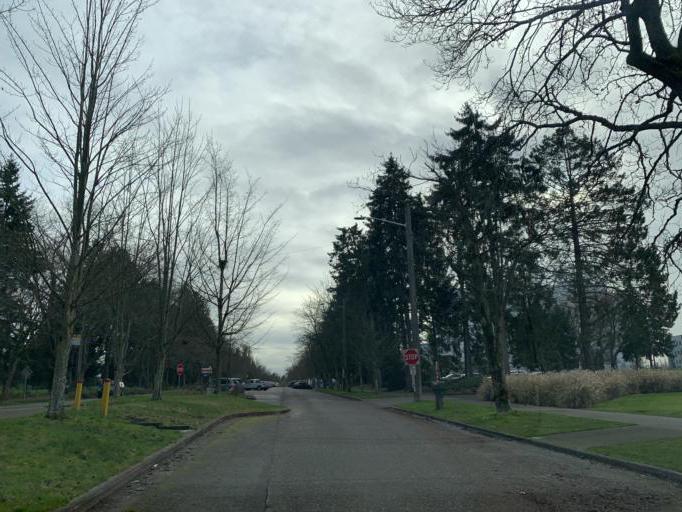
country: US
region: Washington
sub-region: King County
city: Seattle
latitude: 47.5671
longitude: -122.3069
